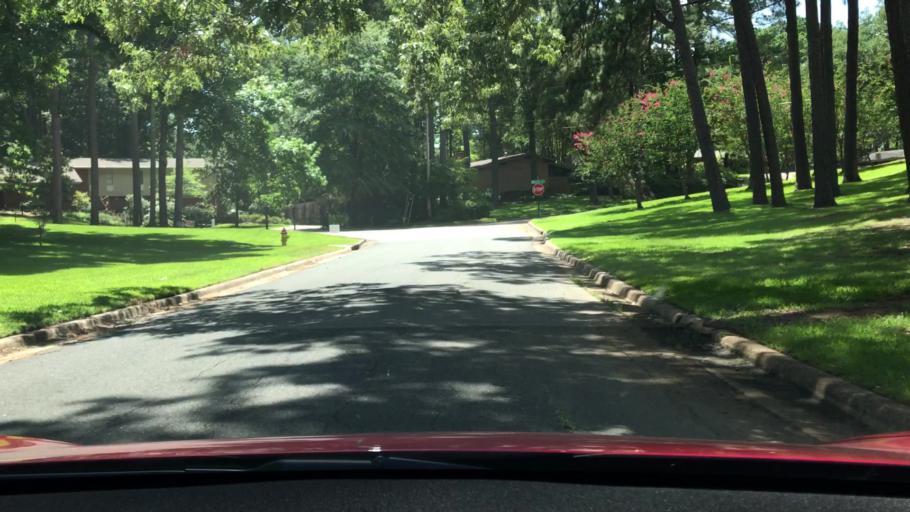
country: US
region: Louisiana
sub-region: Bossier Parish
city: Bossier City
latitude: 32.4320
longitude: -93.7321
